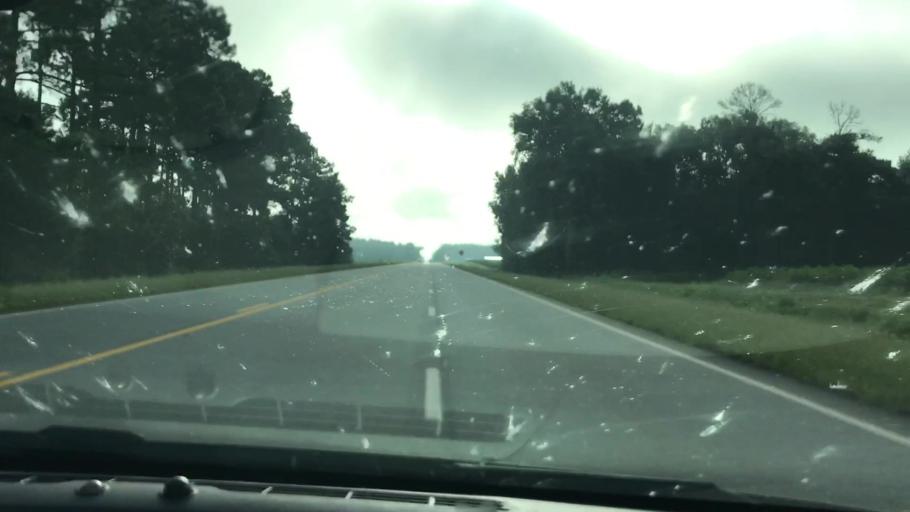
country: US
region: Georgia
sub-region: Randolph County
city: Shellman
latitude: 31.7706
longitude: -84.5451
